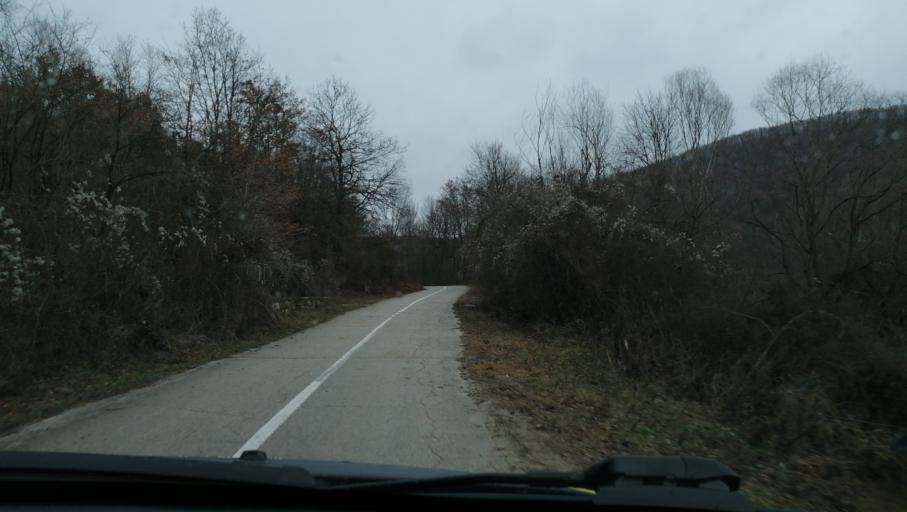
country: RS
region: Central Serbia
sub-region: Pirotski Okrug
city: Dimitrovgrad
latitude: 42.9659
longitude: 22.7837
